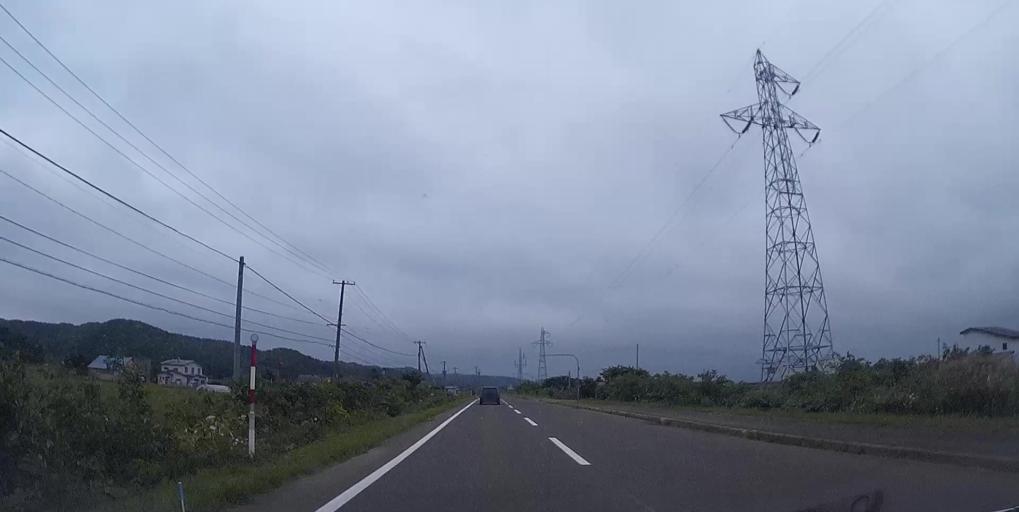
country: JP
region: Hokkaido
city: Iwanai
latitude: 42.4255
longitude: 139.9071
